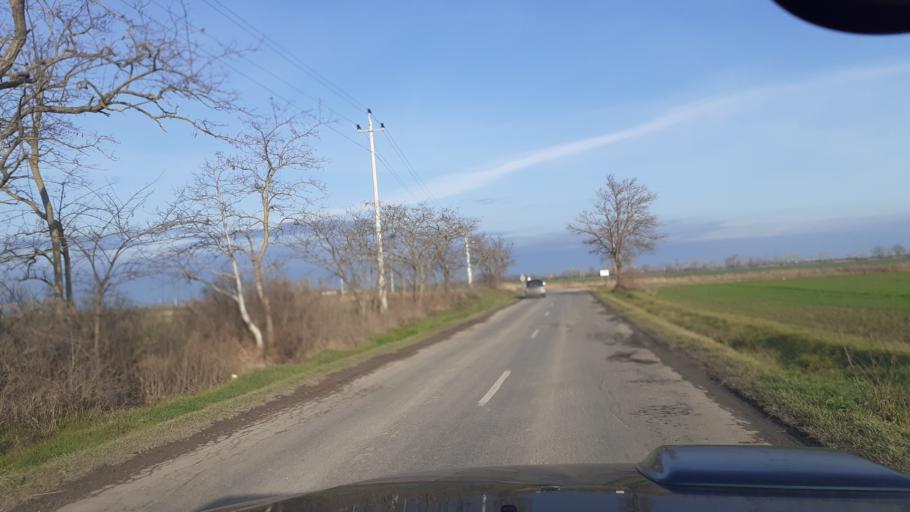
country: HU
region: Pest
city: Domsod
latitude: 47.0925
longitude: 19.0433
